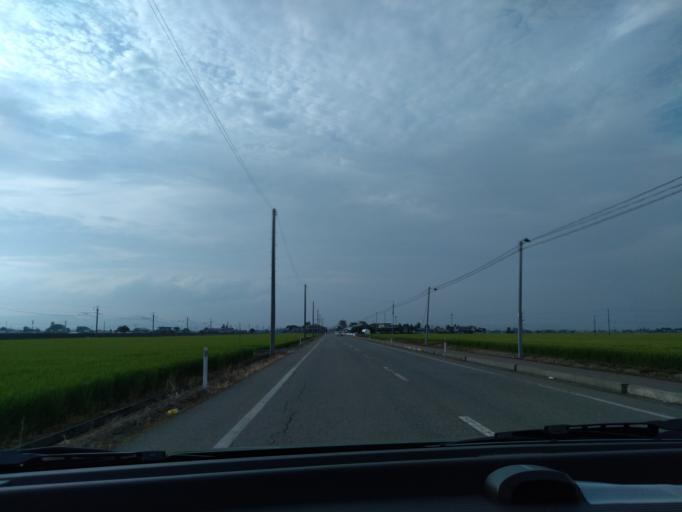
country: JP
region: Akita
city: Omagari
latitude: 39.3944
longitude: 140.5228
